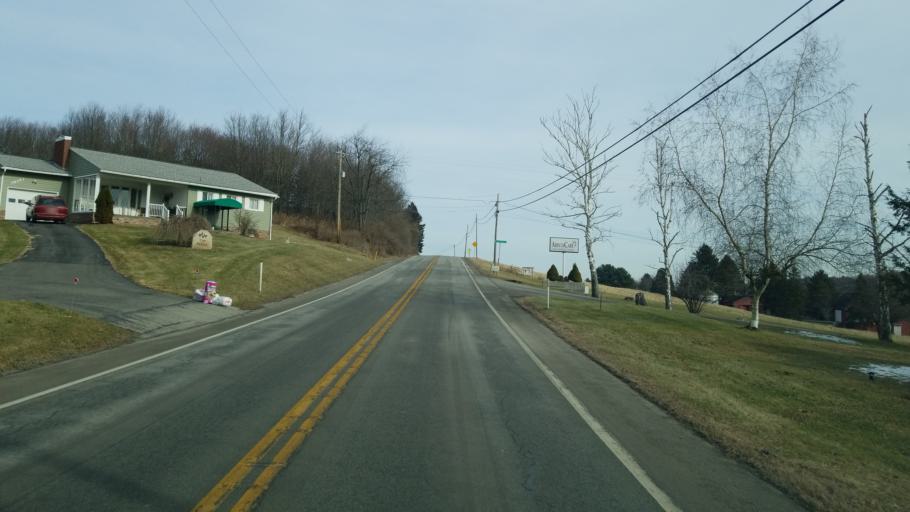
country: US
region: Pennsylvania
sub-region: Indiana County
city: Johnsonburg
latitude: 40.7479
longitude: -78.8914
